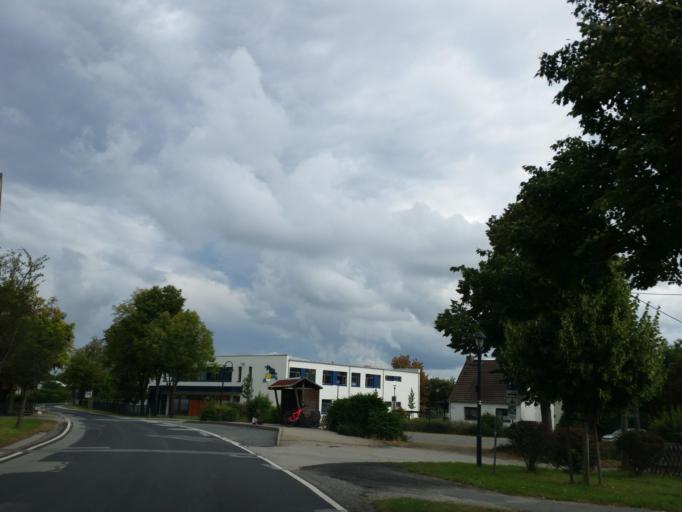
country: DE
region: Saxony
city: Weissenberg
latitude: 51.1961
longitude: 14.6635
